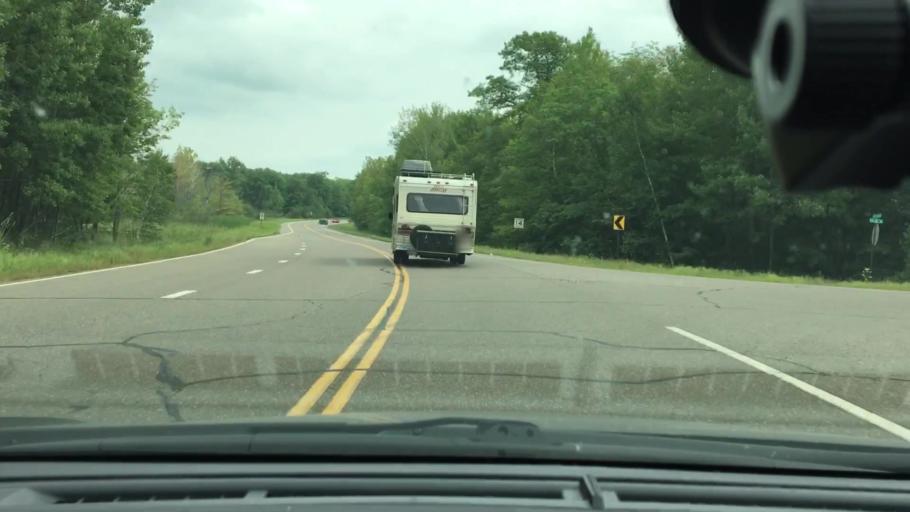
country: US
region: Minnesota
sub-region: Crow Wing County
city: Crosby
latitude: 46.4102
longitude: -93.8352
